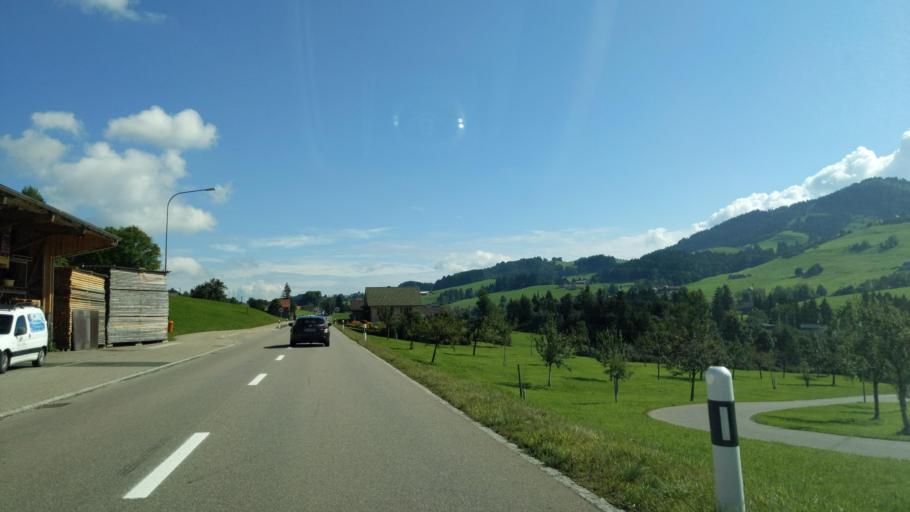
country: CH
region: Saint Gallen
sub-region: Wahlkreis Toggenburg
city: Sankt Peterzell
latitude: 47.3247
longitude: 9.2099
